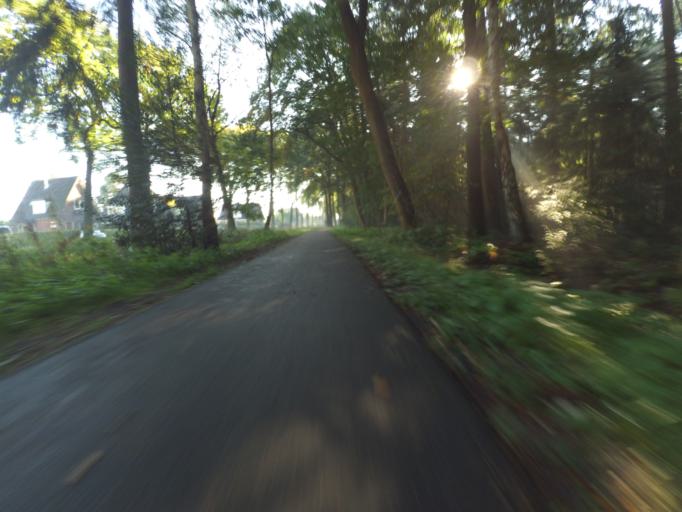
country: NL
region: Gelderland
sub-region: Gemeente Apeldoorn
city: Apeldoorn
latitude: 52.2441
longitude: 5.9500
